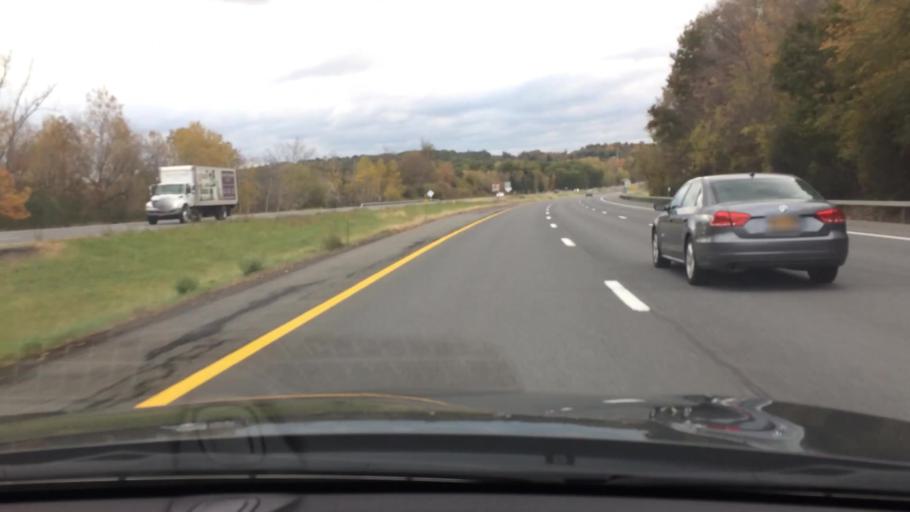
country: US
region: New York
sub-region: Rensselaer County
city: Hampton Manor
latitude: 42.6239
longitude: -73.6948
